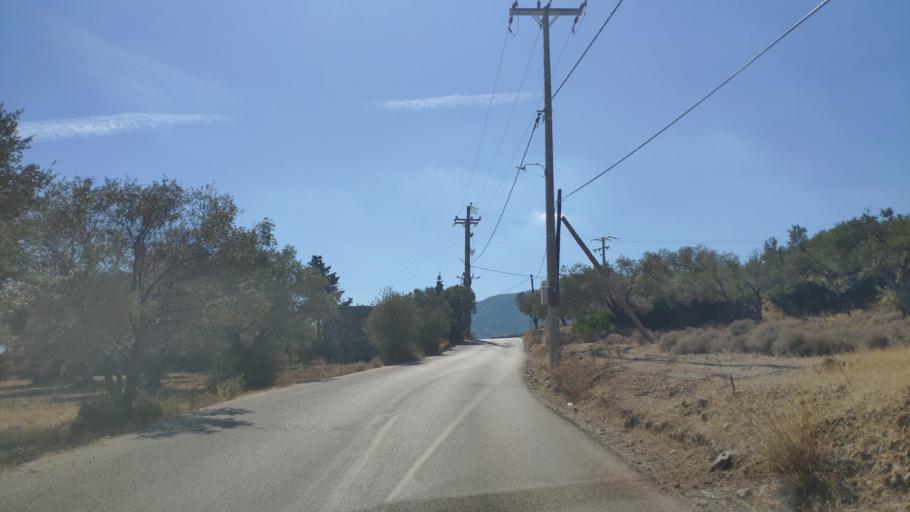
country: GR
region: Attica
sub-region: Nomarchia Anatolikis Attikis
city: Keratea
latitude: 37.8223
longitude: 23.9930
